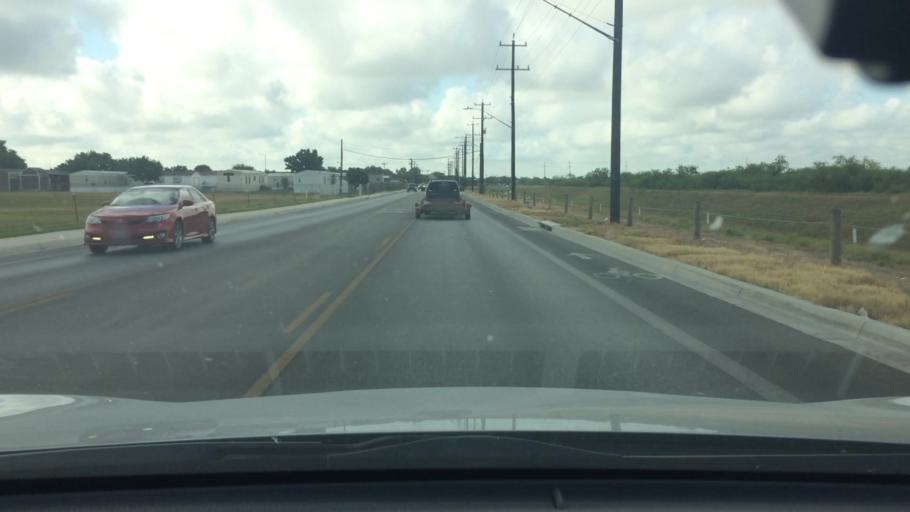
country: US
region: Texas
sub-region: Bexar County
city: China Grove
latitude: 29.3433
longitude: -98.4258
